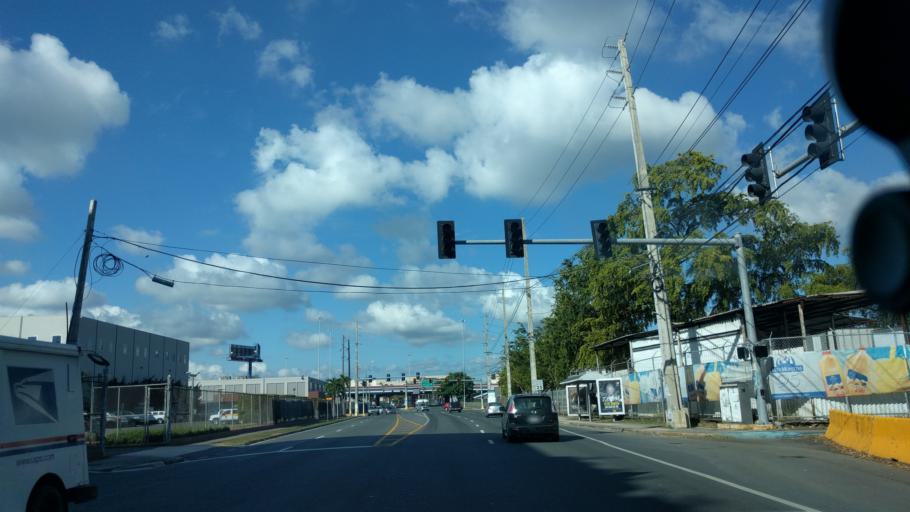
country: PR
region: Catano
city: Catano
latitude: 18.4236
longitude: -66.0689
